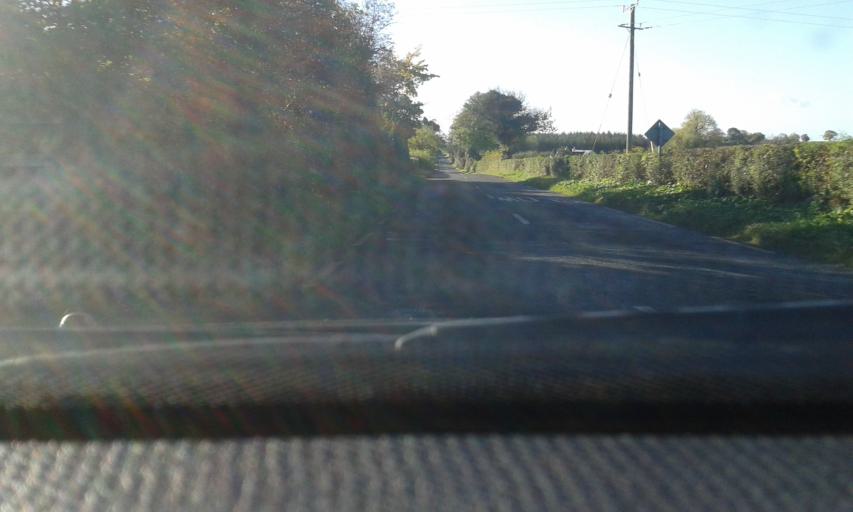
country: IE
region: Leinster
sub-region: Kildare
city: Monasterevin
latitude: 53.1679
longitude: -7.0328
